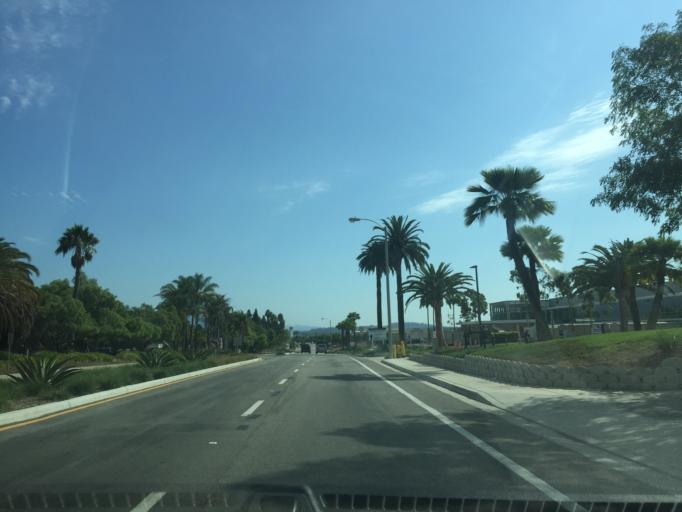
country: US
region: California
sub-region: Santa Barbara County
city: Isla Vista
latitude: 34.4302
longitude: -119.8670
